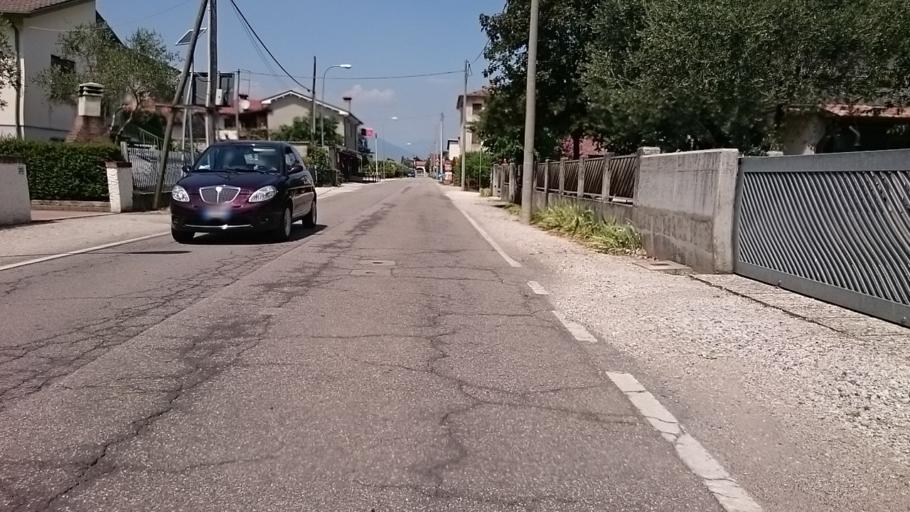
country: IT
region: Veneto
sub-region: Provincia di Padova
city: Fontaniva
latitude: 45.6586
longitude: 11.7572
